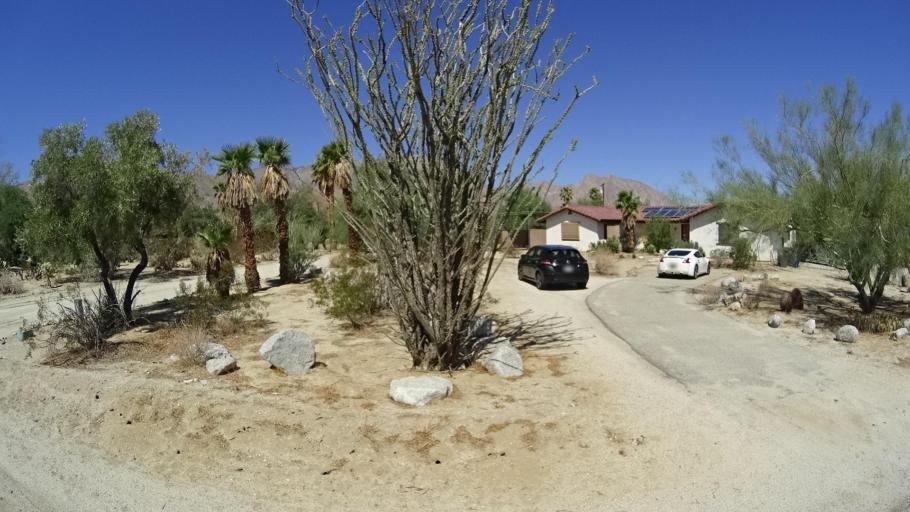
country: US
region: California
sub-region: San Diego County
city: Borrego Springs
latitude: 33.2298
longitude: -116.3841
